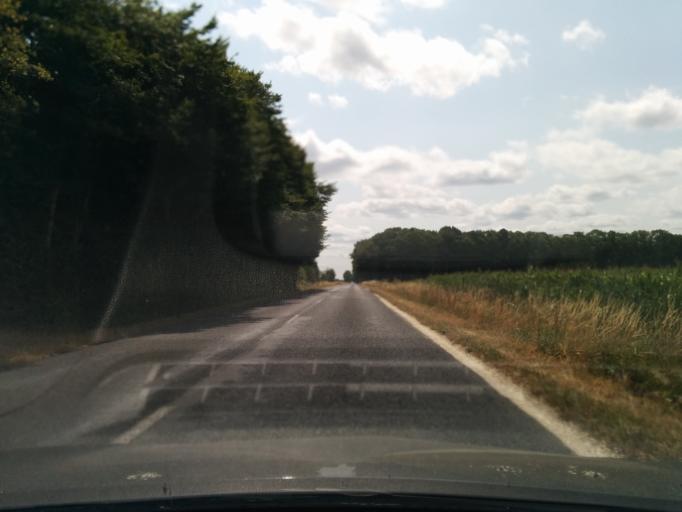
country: FR
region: Centre
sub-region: Departement du Cher
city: Henrichemont
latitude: 47.3506
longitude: 2.4043
